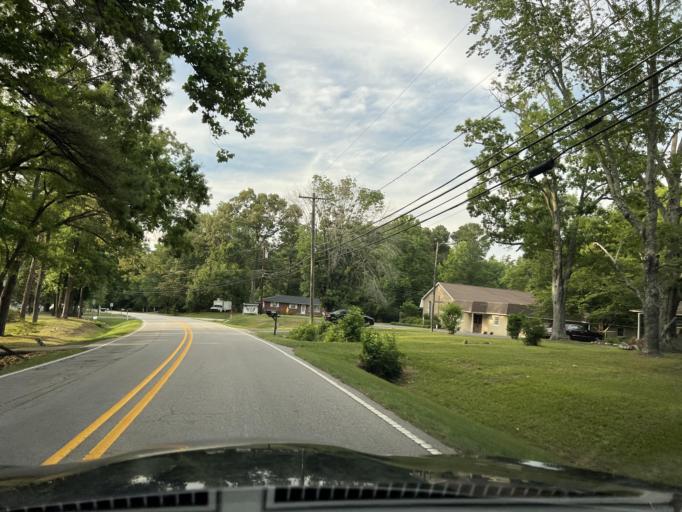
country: US
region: North Carolina
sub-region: Durham County
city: Durham
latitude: 35.9788
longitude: -78.8412
